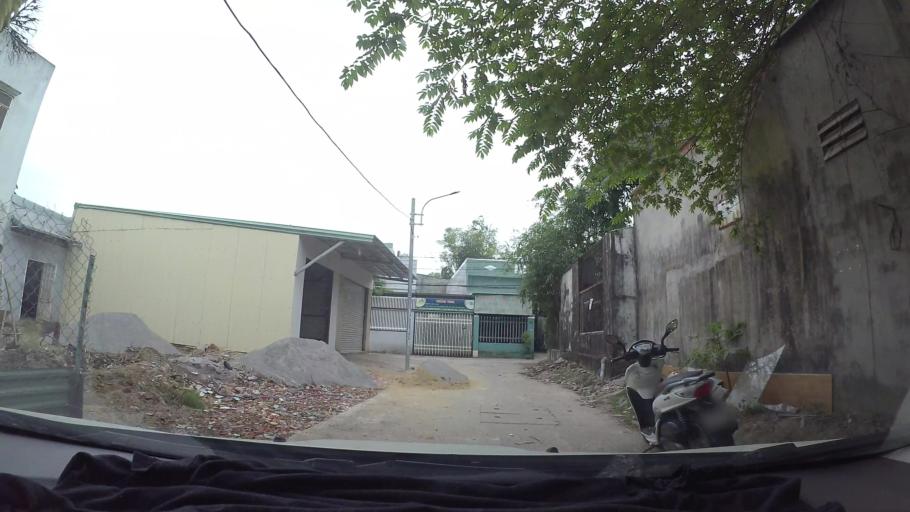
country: VN
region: Da Nang
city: Lien Chieu
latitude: 16.0623
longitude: 108.1684
